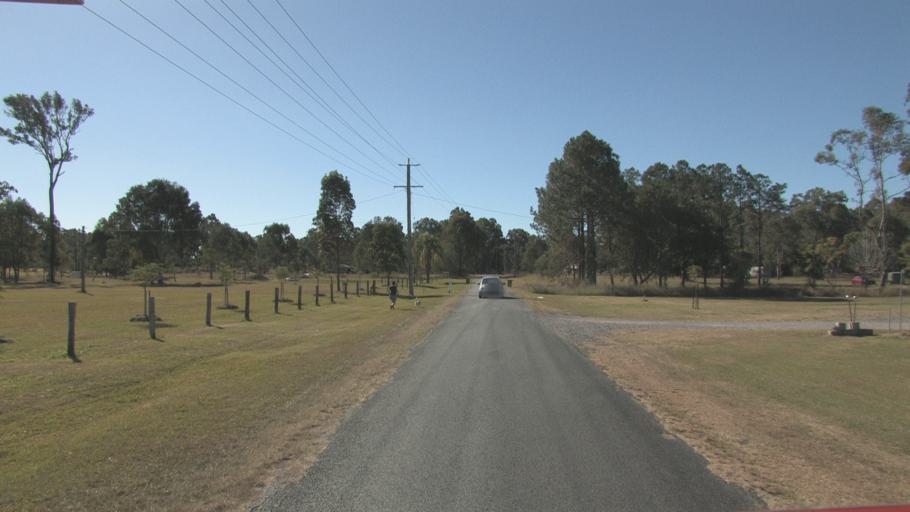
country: AU
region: Queensland
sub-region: Logan
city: North Maclean
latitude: -27.7785
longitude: 153.0194
